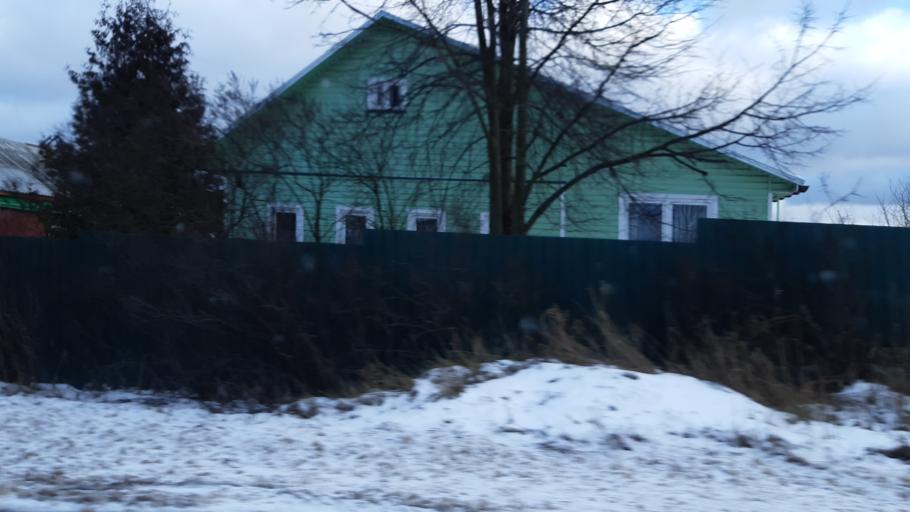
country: RU
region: Moskovskaya
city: Noginsk-9
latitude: 55.9892
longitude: 38.5421
